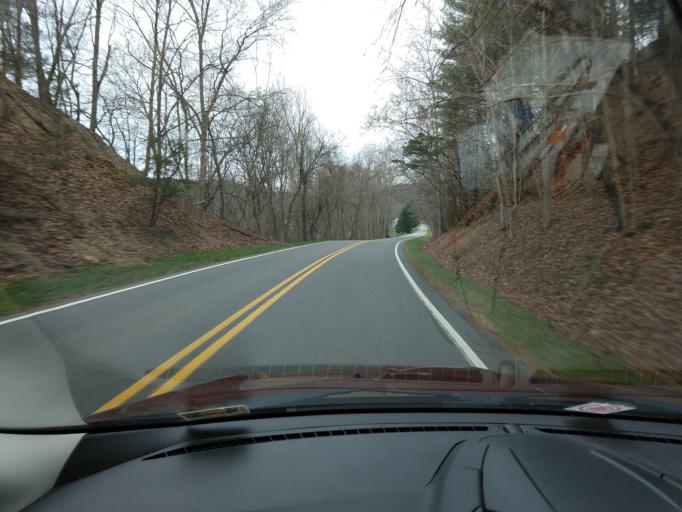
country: US
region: West Virginia
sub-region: Greenbrier County
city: White Sulphur Springs
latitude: 37.7461
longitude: -80.1705
